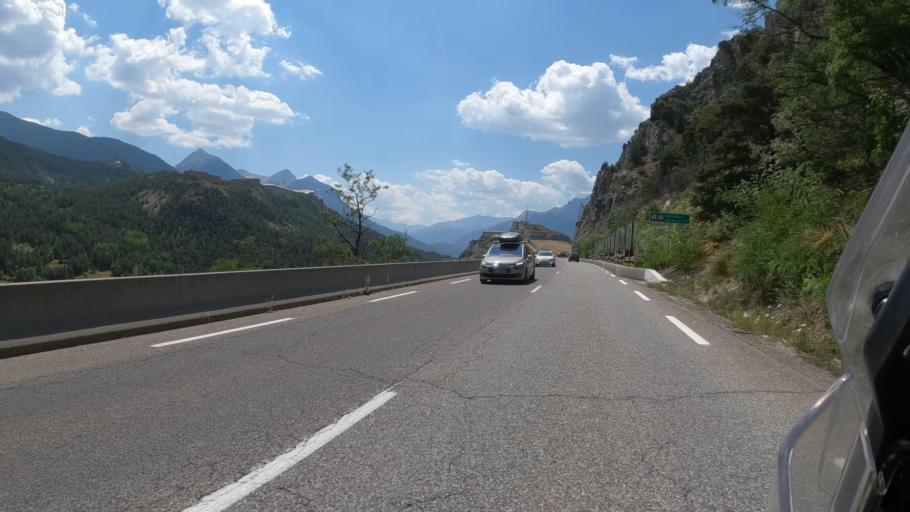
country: IT
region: Piedmont
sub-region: Provincia di Torino
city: Claviere
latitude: 44.9304
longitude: 6.7215
